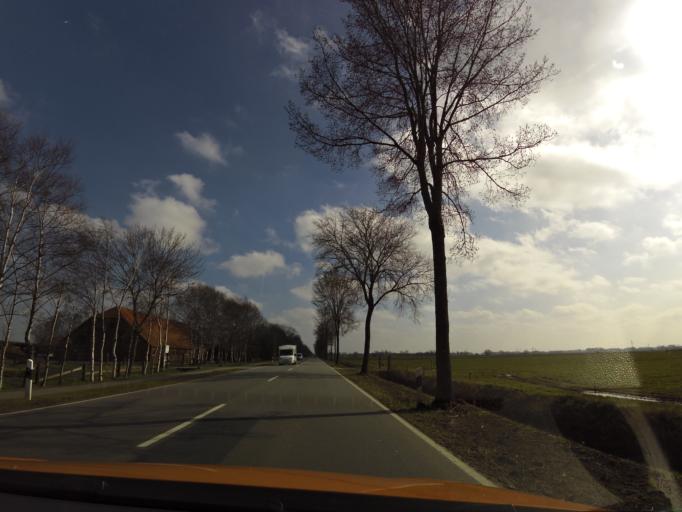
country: DE
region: Lower Saxony
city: Varel
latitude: 53.3867
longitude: 8.2116
